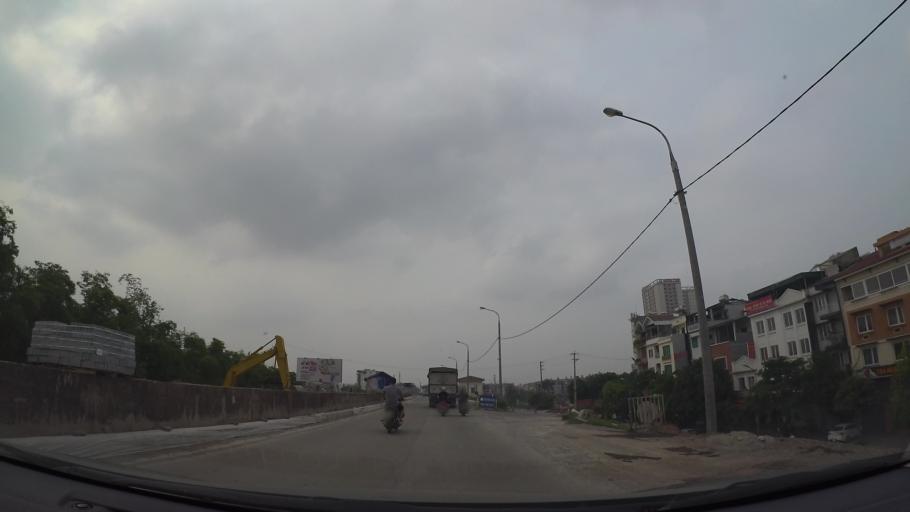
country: VN
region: Ha Noi
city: Trau Quy
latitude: 21.0159
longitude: 105.9047
